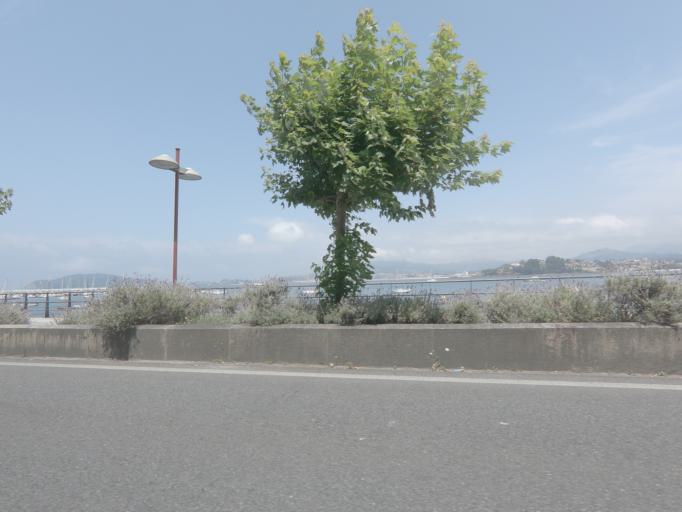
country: ES
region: Galicia
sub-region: Provincia de Pontevedra
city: Baiona
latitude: 42.1159
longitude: -8.8428
